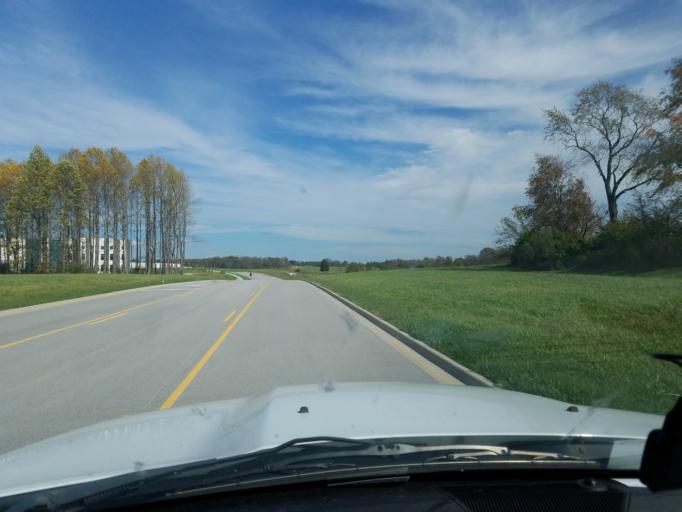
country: US
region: Indiana
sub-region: Clark County
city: Charlestown
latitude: 38.3823
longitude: -85.6794
